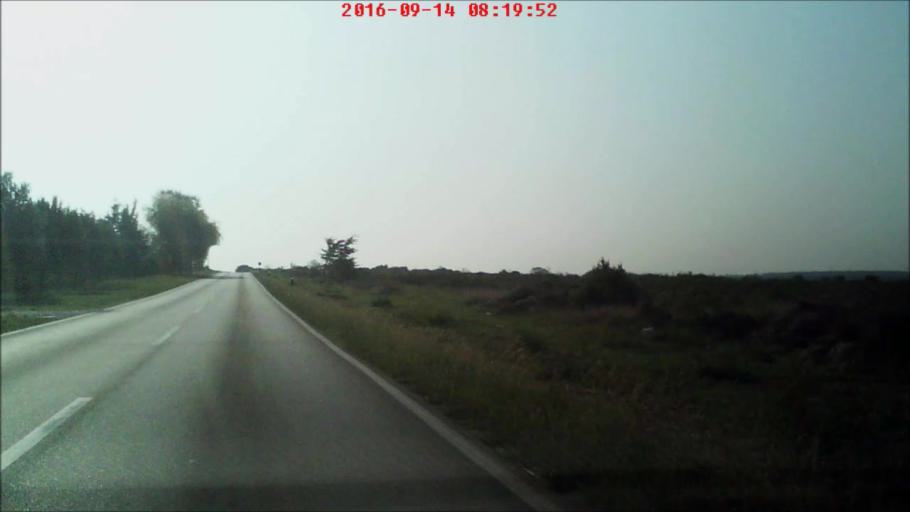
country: HR
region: Zadarska
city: Nin
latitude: 44.2297
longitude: 15.1949
